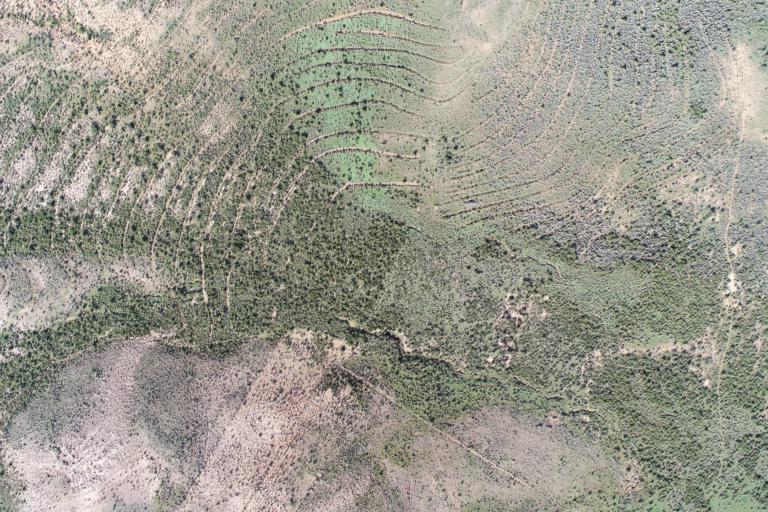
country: BO
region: La Paz
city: Curahuara de Carangas
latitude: -17.3034
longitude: -68.5064
